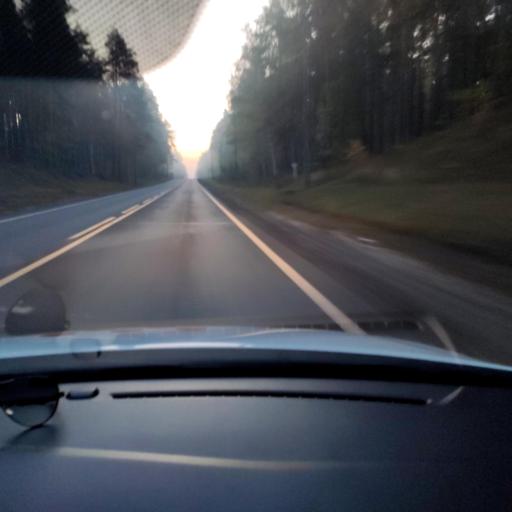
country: RU
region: Tatarstan
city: Verkhniy Uslon
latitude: 55.6386
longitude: 49.0386
